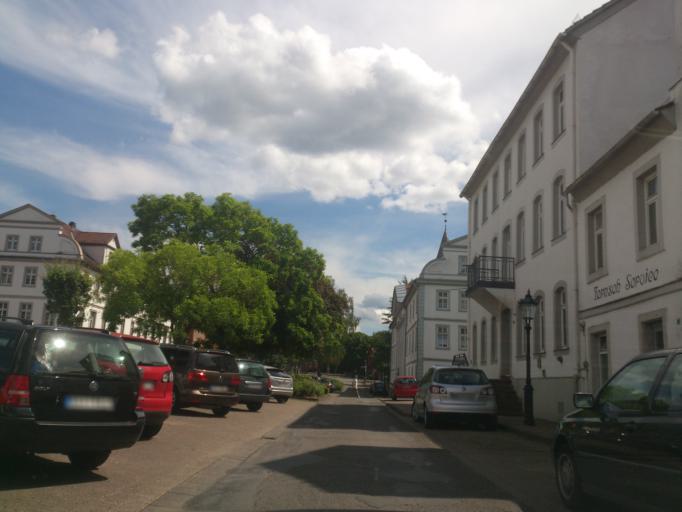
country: DE
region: Lower Saxony
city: Bad Karlshafen
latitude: 51.6408
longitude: 9.4509
